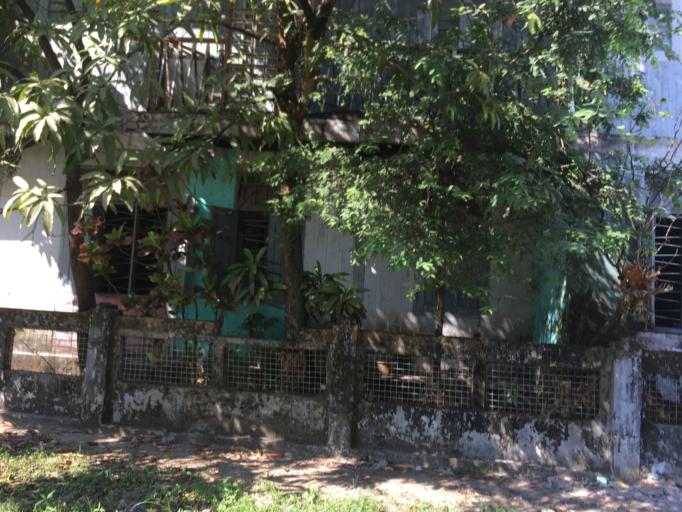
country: MM
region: Mon
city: Mawlamyine
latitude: 16.4964
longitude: 97.6355
